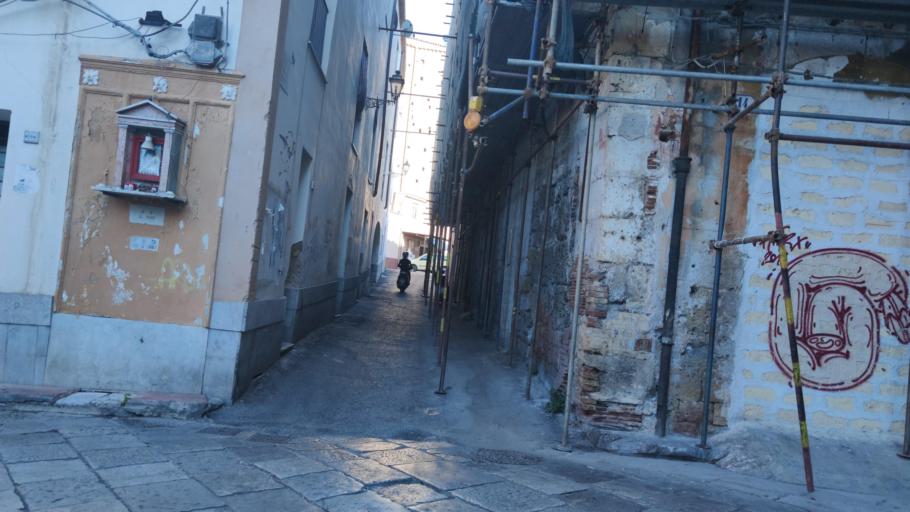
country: IT
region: Sicily
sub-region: Palermo
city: Palermo
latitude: 38.1113
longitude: 13.3608
